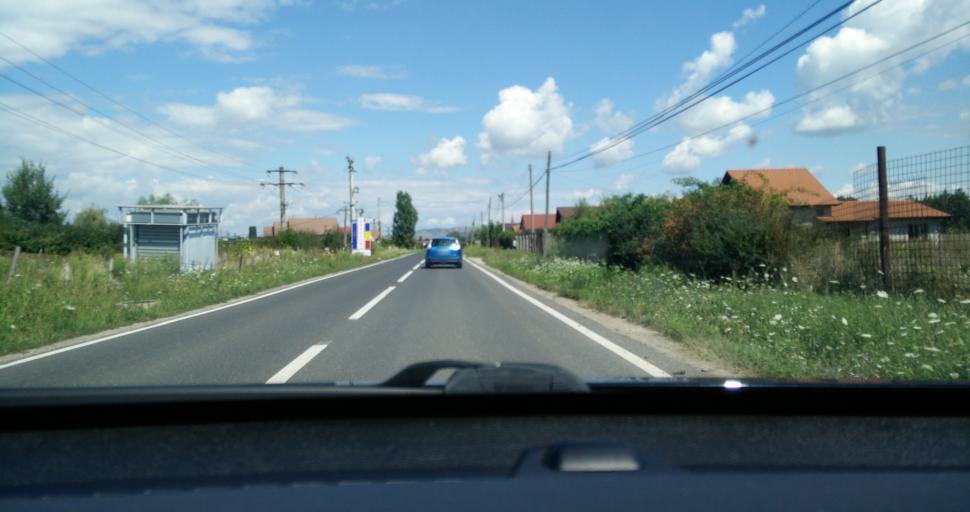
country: RO
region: Alba
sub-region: Municipiul Sebes
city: Petresti
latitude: 45.9124
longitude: 23.5543
